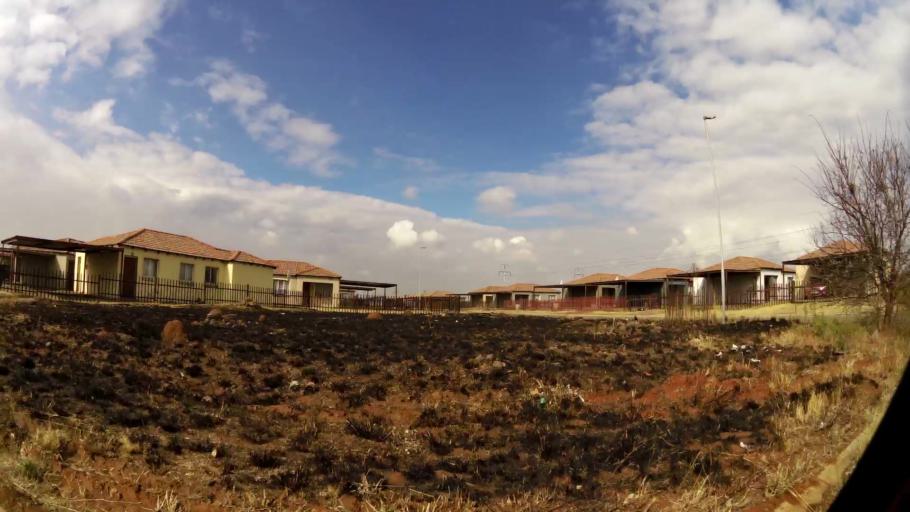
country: ZA
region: Gauteng
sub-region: Sedibeng District Municipality
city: Vanderbijlpark
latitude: -26.7165
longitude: 27.8820
